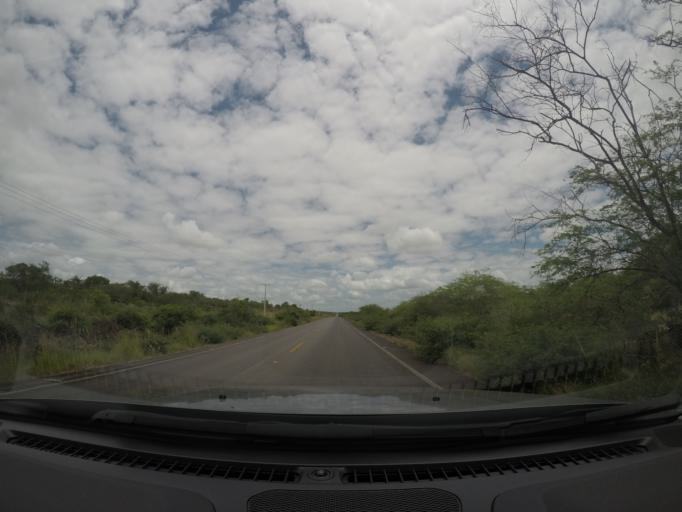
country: BR
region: Bahia
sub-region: Itaberaba
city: Itaberaba
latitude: -12.4713
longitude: -40.1885
